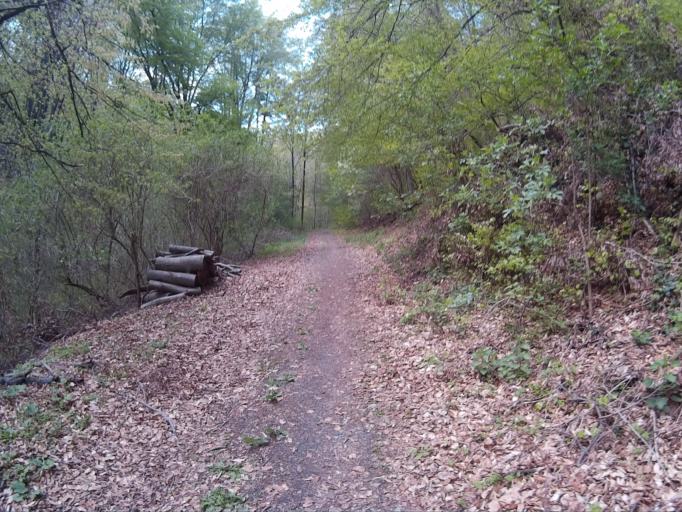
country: AT
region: Burgenland
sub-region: Politischer Bezirk Oberwart
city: Rechnitz
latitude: 47.3499
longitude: 16.4722
